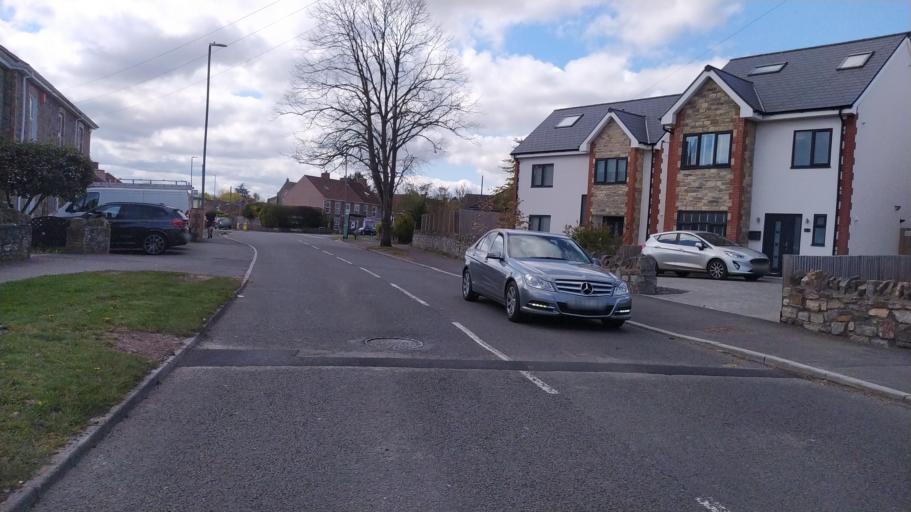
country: GB
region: England
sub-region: South Gloucestershire
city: Kingswood
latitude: 51.4406
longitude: -2.4924
